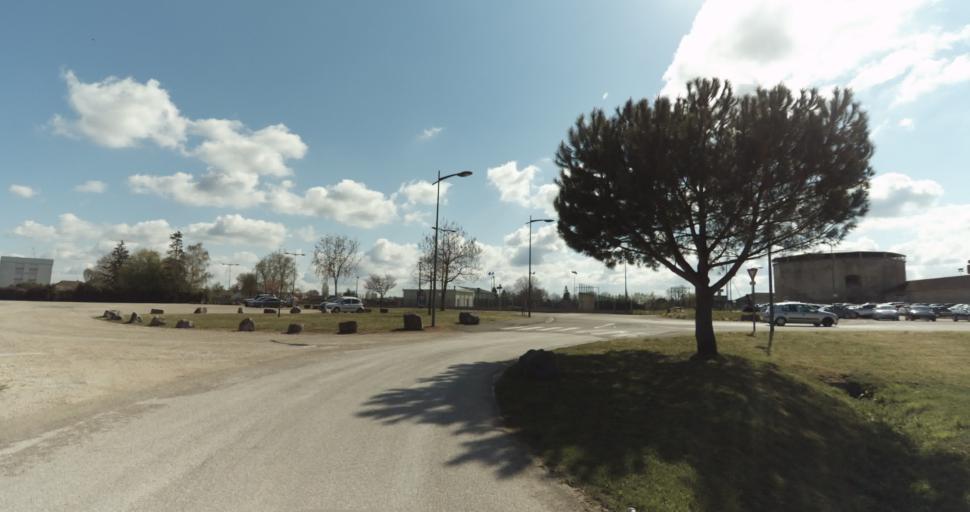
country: FR
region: Bourgogne
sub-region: Departement de la Cote-d'Or
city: Auxonne
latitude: 47.1977
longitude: 5.3906
